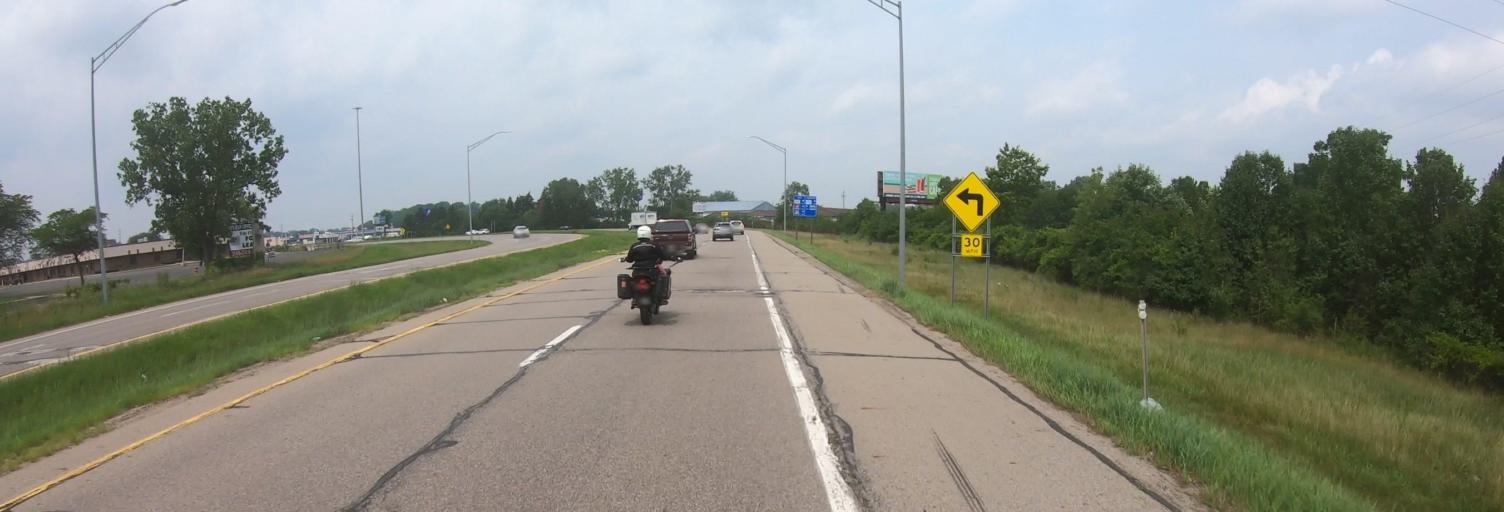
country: US
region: Michigan
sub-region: Ingham County
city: Holt
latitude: 42.6644
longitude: -84.5338
